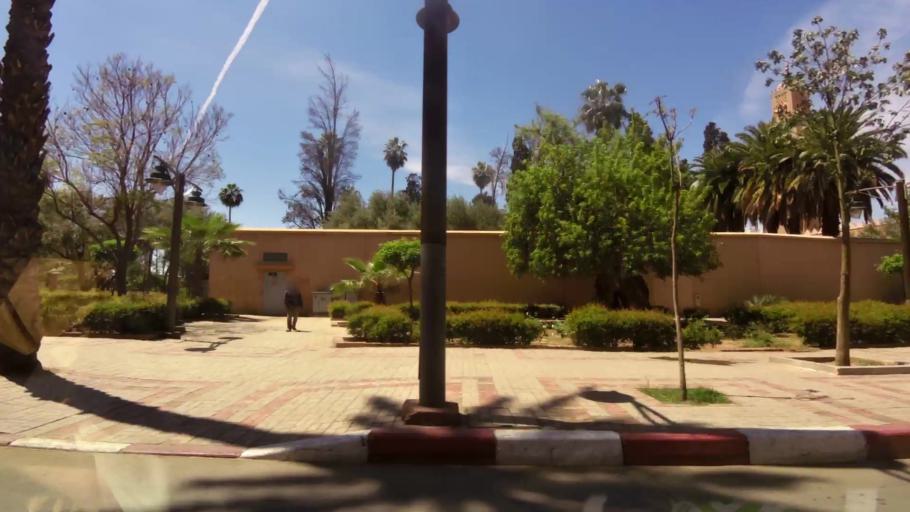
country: MA
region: Marrakech-Tensift-Al Haouz
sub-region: Marrakech
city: Marrakesh
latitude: 31.6234
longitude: -7.9919
